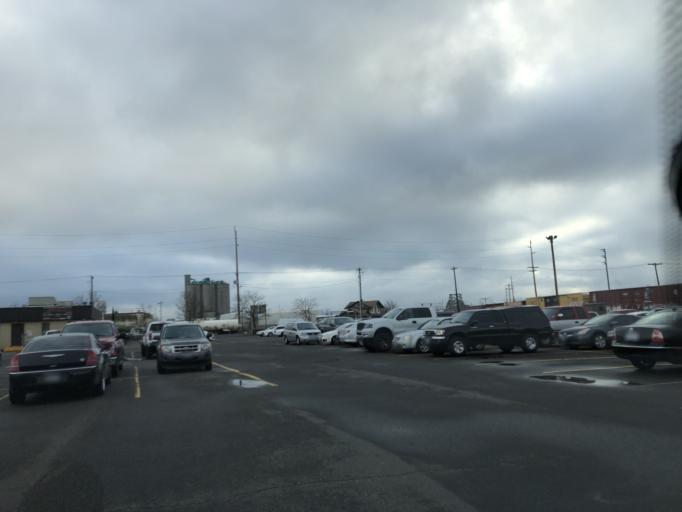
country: US
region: Washington
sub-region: Clark County
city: Vancouver
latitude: 45.6307
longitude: -122.6854
